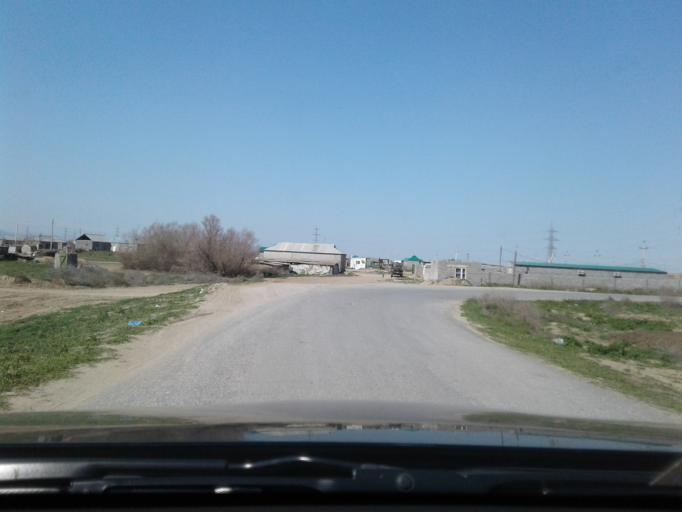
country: TM
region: Ahal
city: Abadan
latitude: 38.1090
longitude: 58.2042
